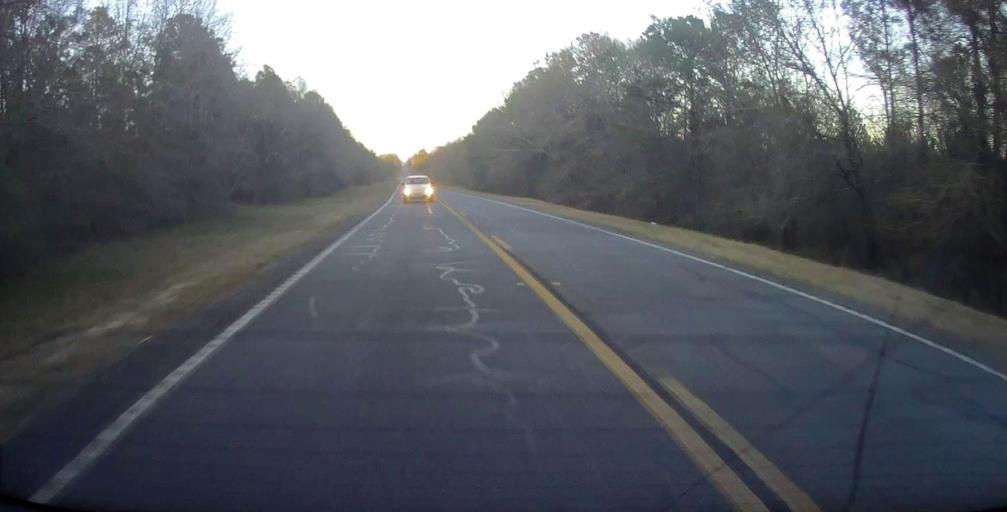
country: US
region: Georgia
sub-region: Dodge County
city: Eastman
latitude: 32.2671
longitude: -83.1262
